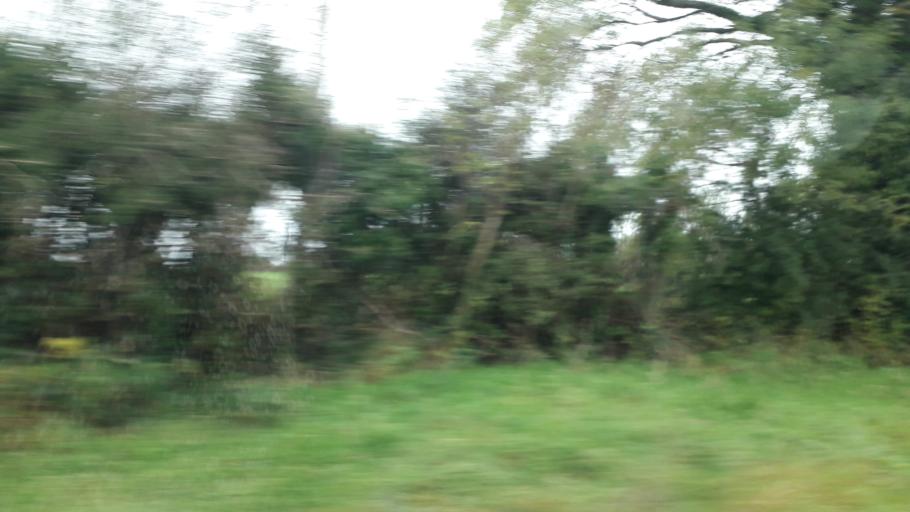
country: IE
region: Connaught
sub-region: Roscommon
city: Ballaghaderreen
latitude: 53.8959
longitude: -8.5625
